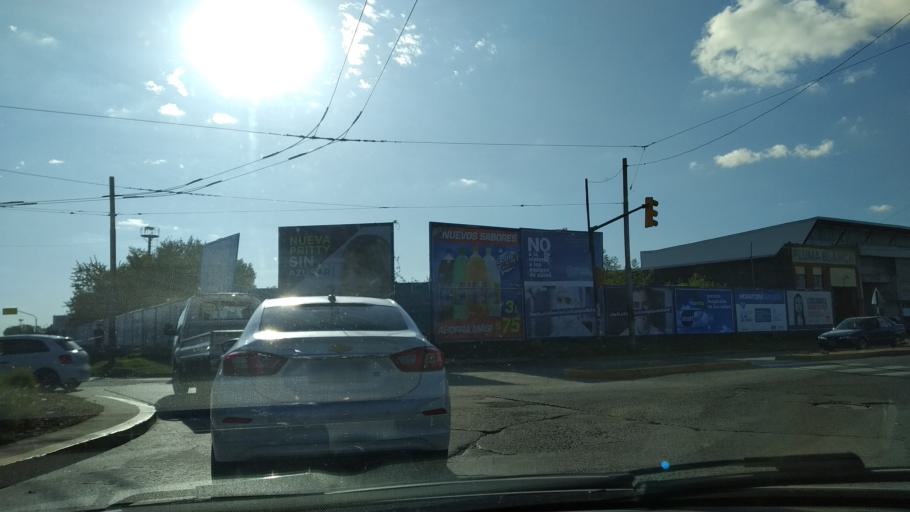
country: AR
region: Santa Fe
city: Perez
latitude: -32.9403
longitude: -60.7383
